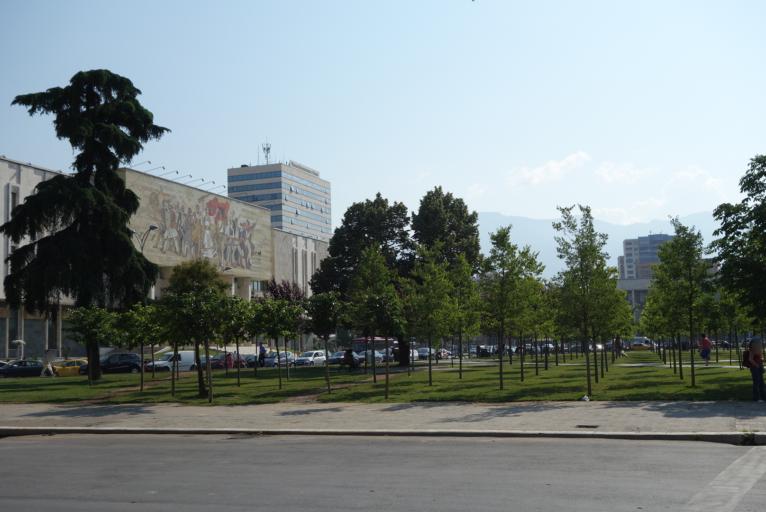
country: AL
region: Tirane
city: Tirana
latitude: 41.3282
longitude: 19.8160
